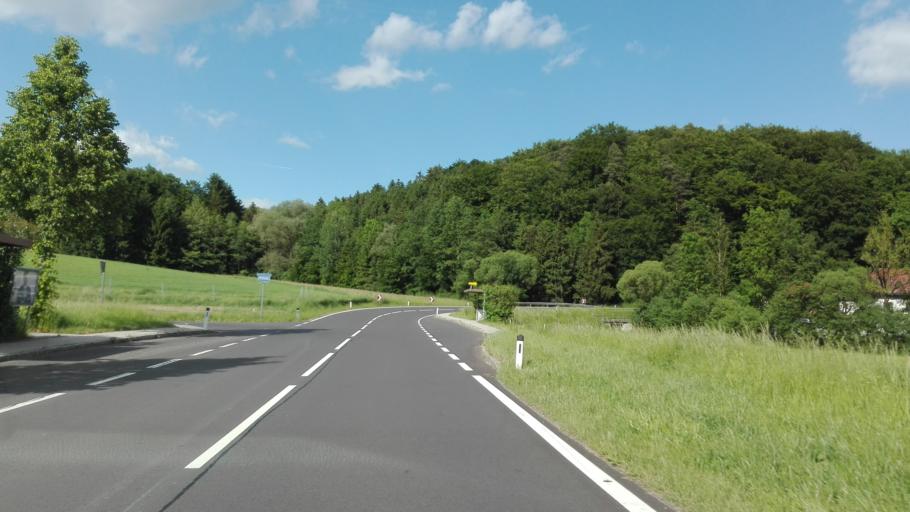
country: AT
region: Upper Austria
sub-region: Politischer Bezirk Urfahr-Umgebung
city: Gallneukirchen
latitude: 48.3376
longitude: 14.3771
